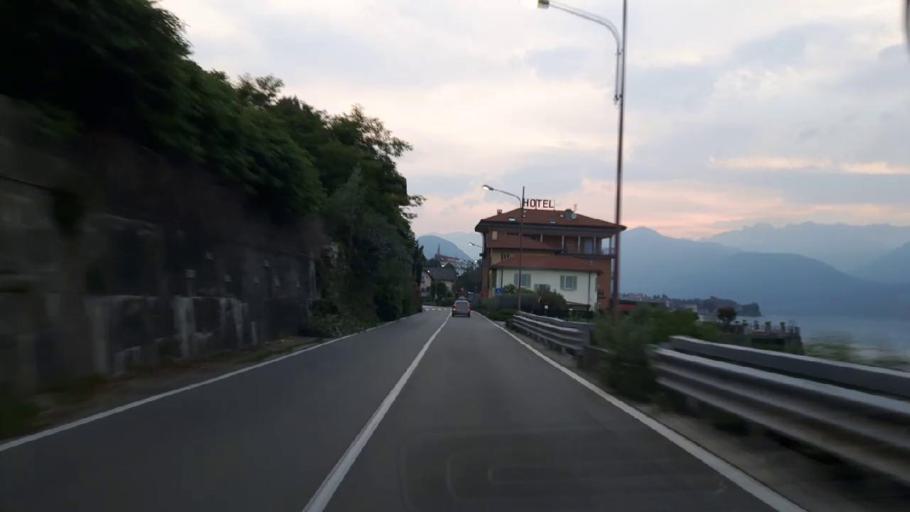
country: IT
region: Piedmont
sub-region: Provincia Verbano-Cusio-Ossola
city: Baveno
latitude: 45.8984
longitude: 8.5125
